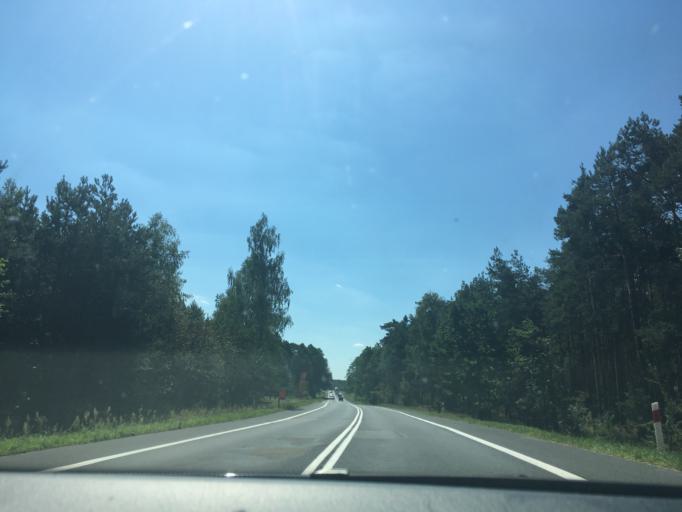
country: PL
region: Subcarpathian Voivodeship
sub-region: Powiat nizanski
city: Jarocin
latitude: 50.5998
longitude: 22.2767
